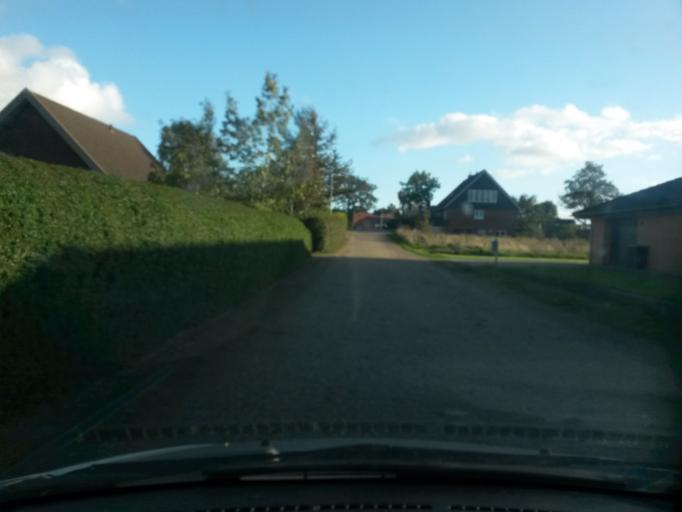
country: DK
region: Central Jutland
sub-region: Viborg Kommune
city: Viborg
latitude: 56.3768
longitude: 9.3913
